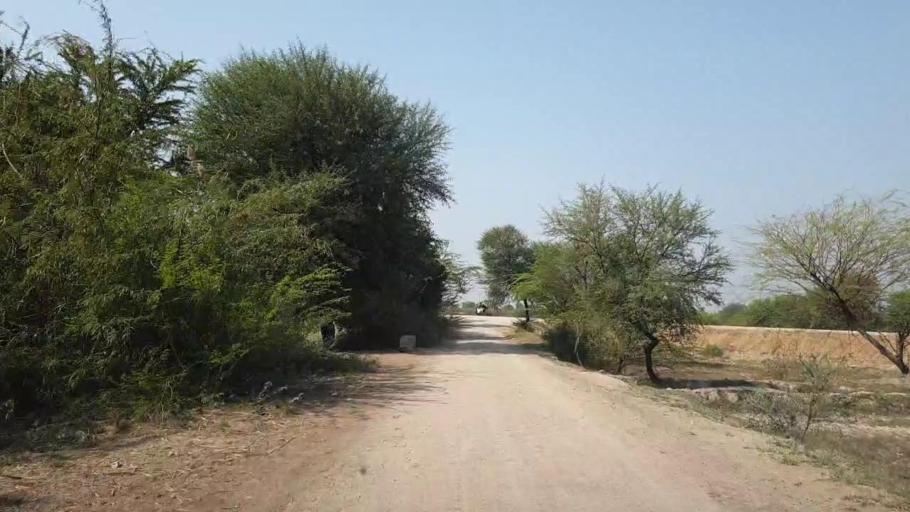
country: PK
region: Sindh
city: Mirpur Khas
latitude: 25.6236
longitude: 69.0903
